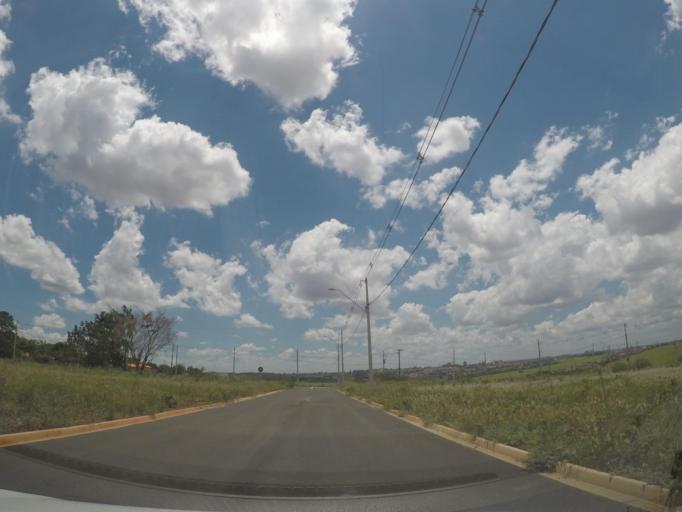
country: BR
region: Sao Paulo
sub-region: Hortolandia
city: Hortolandia
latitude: -22.8392
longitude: -47.2338
